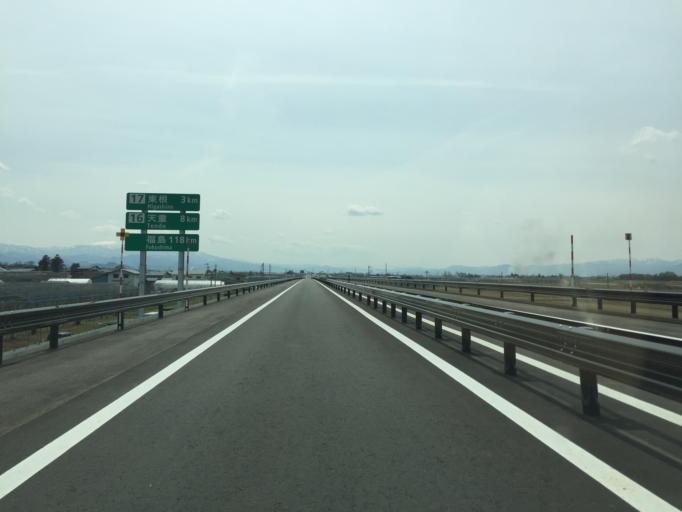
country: JP
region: Yamagata
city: Higashine
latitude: 38.4344
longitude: 140.3535
